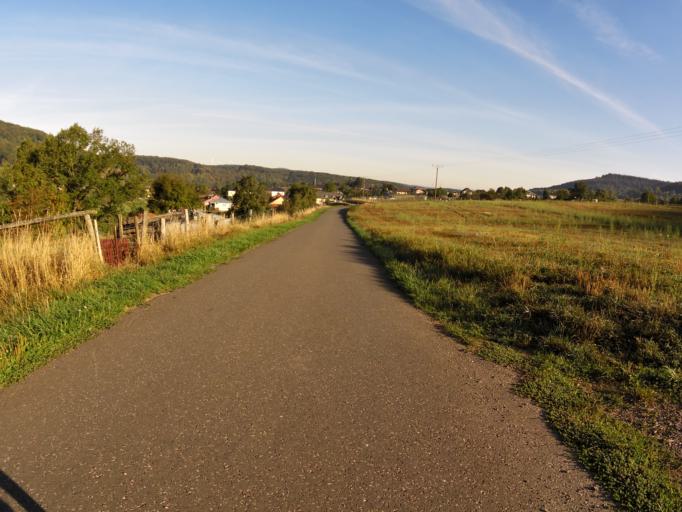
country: DE
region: Rheinland-Pfalz
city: Holsthum
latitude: 49.9045
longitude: 6.4113
